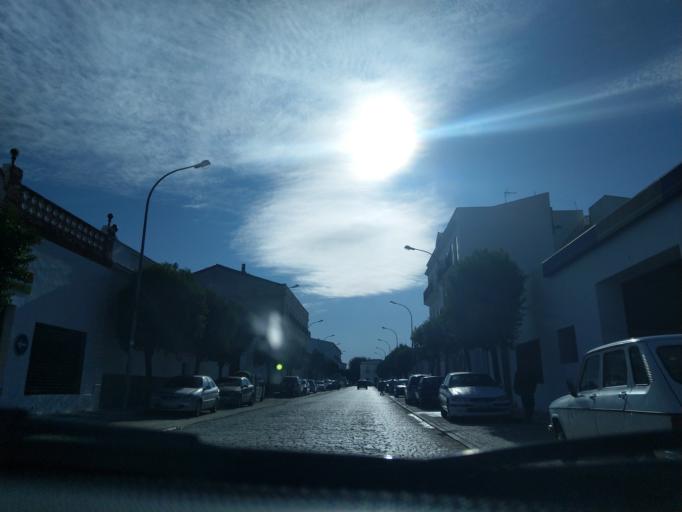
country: ES
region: Extremadura
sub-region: Provincia de Badajoz
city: Llerena
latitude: 38.2384
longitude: -6.0121
